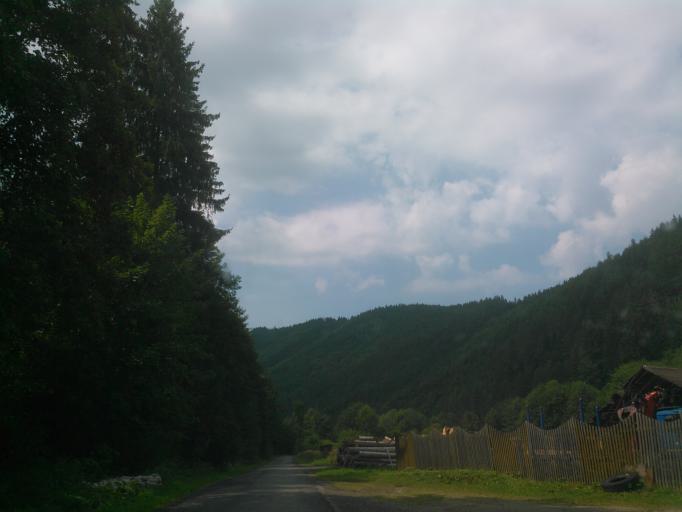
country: SK
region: Zilinsky
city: Ruzomberok
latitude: 49.0441
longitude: 19.4237
